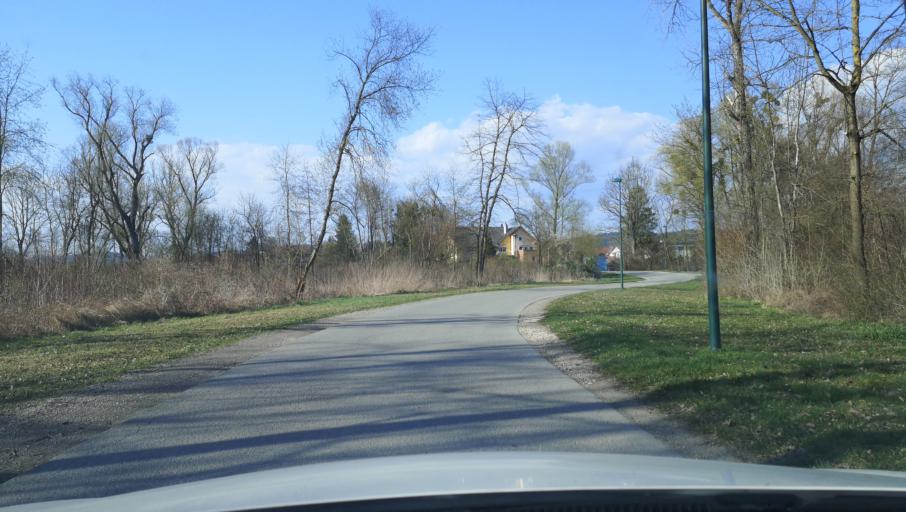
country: AT
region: Lower Austria
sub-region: Politischer Bezirk Melk
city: Blindenmarkt
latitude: 48.1192
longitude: 14.9890
